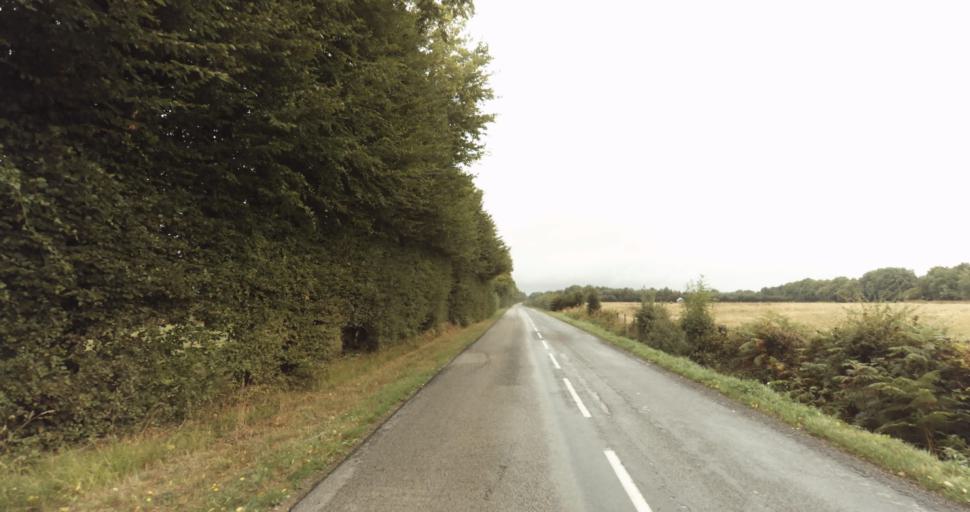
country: FR
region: Lower Normandy
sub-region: Departement de l'Orne
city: Vimoutiers
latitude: 48.8690
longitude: 0.1852
